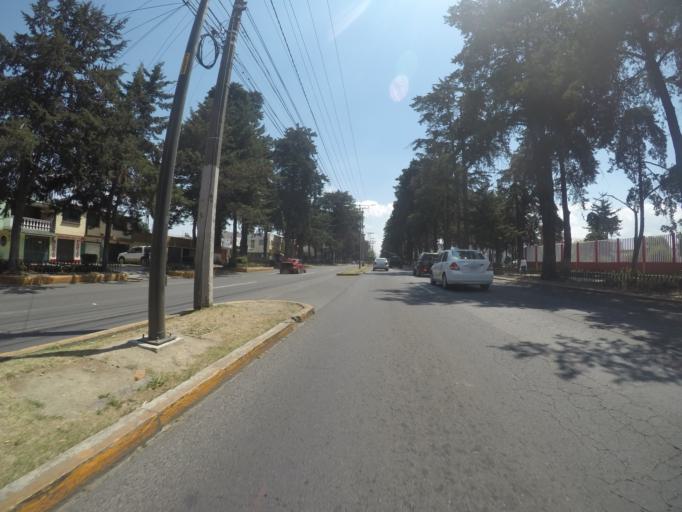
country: MX
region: Mexico
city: San Buenaventura
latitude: 19.2681
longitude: -99.6609
